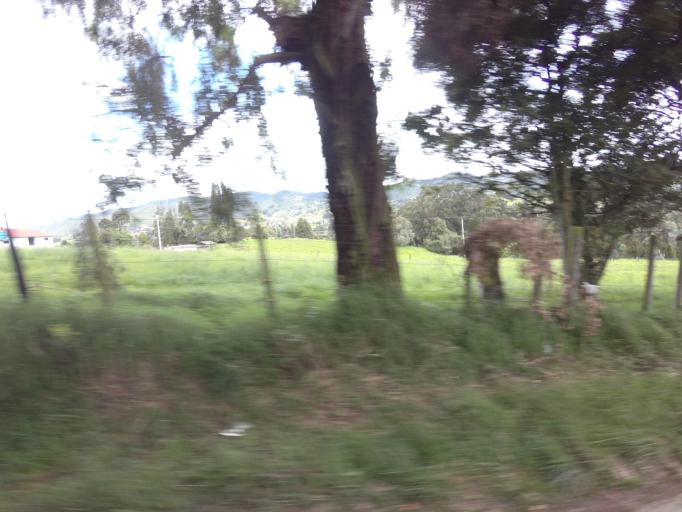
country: CO
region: Cundinamarca
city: Tabio
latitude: 4.9698
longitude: -74.0659
